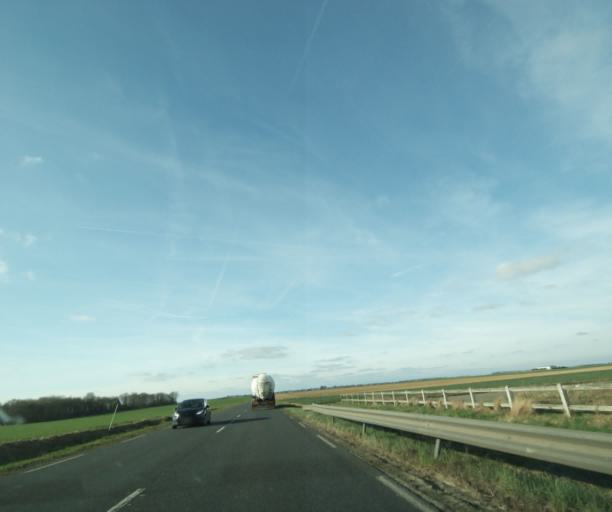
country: FR
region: Ile-de-France
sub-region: Departement des Yvelines
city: Ablis
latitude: 48.4935
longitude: 1.8440
